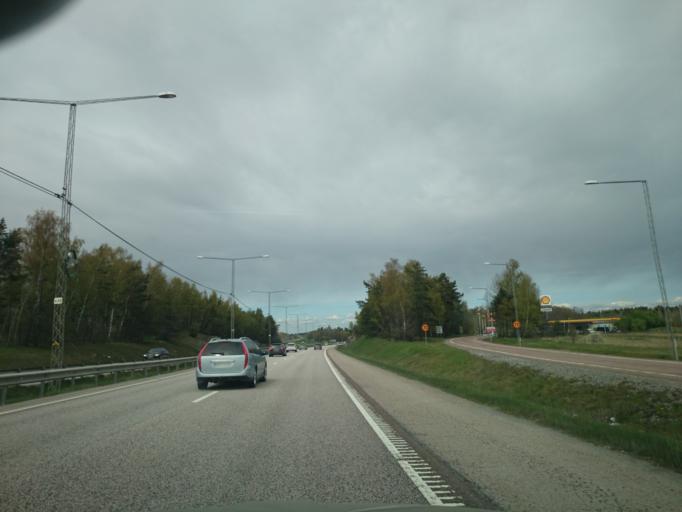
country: SE
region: Stockholm
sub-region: Upplands Vasby Kommun
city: Upplands Vaesby
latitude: 59.5485
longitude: 17.9004
